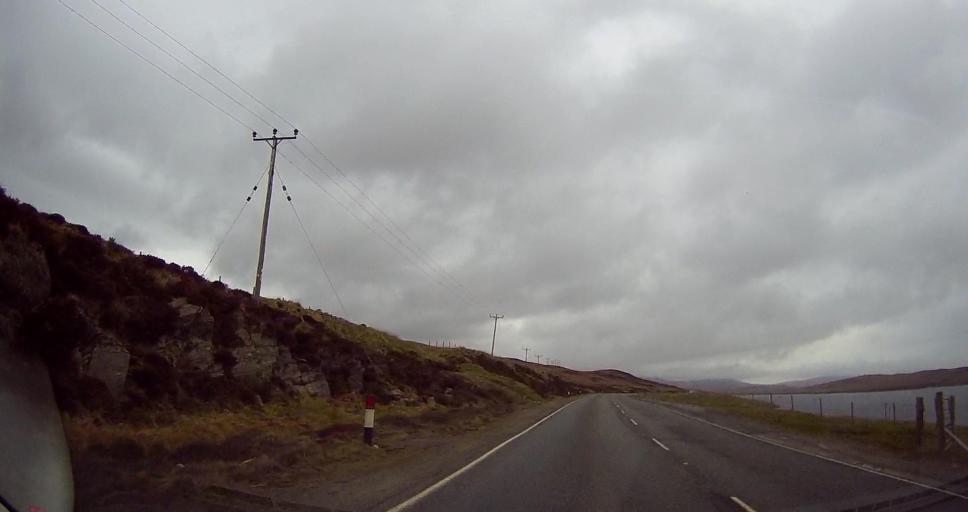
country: GB
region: Scotland
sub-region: Shetland Islands
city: Lerwick
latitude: 60.2439
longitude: -1.2292
